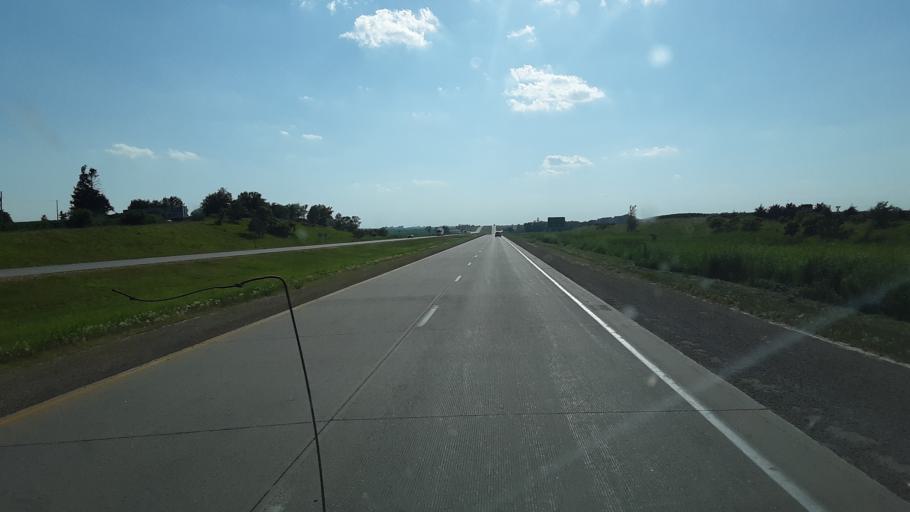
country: US
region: Iowa
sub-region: Grundy County
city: Grundy Center
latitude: 42.4631
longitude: -92.7468
